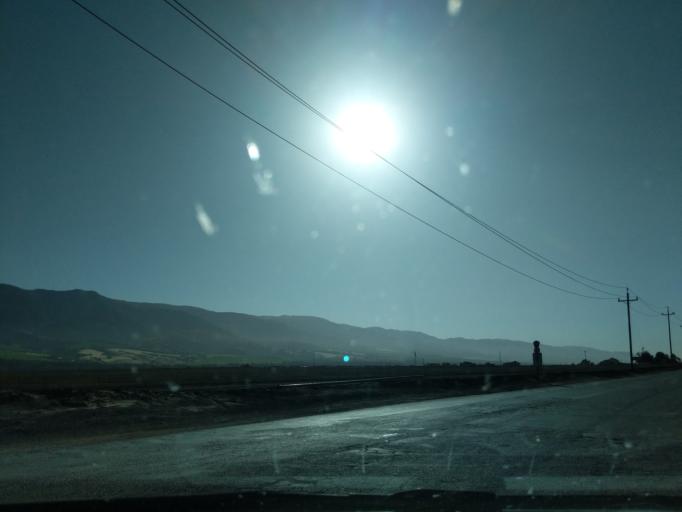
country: US
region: California
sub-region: Monterey County
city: Soledad
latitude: 36.3954
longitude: -121.3334
